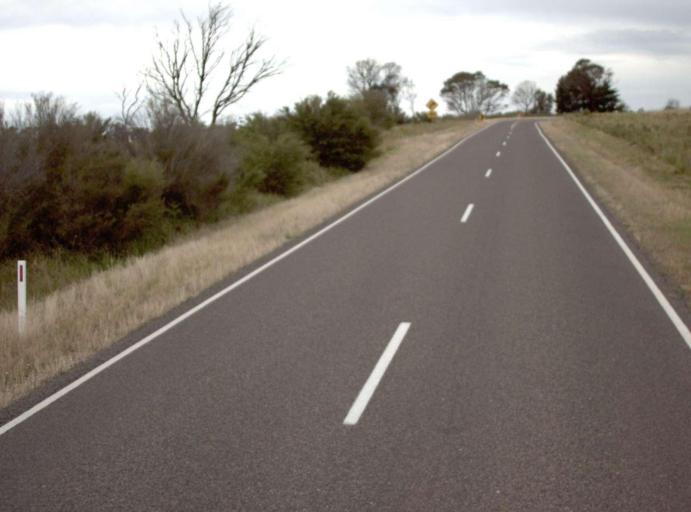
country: AU
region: Victoria
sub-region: East Gippsland
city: Bairnsdale
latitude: -37.9966
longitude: 147.3976
